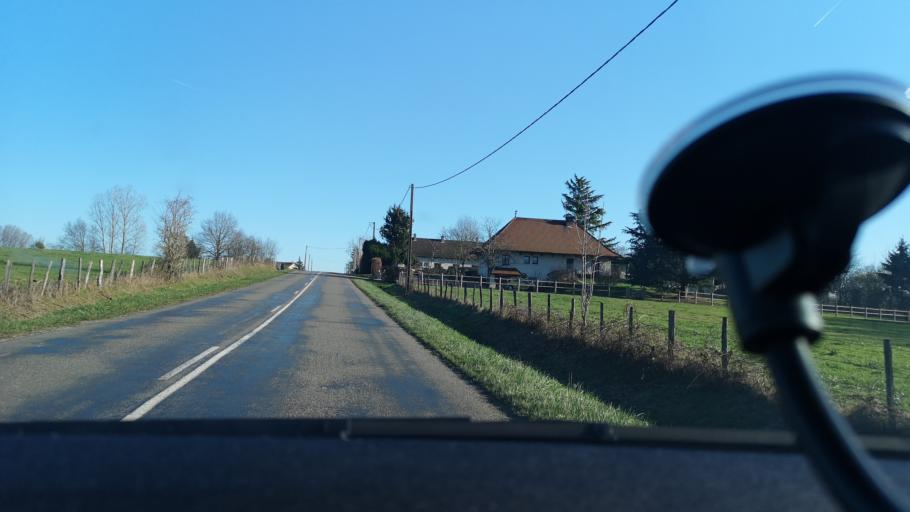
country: FR
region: Bourgogne
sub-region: Departement de Saone-et-Loire
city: Saint-Germain-du-Bois
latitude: 46.7517
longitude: 5.2626
